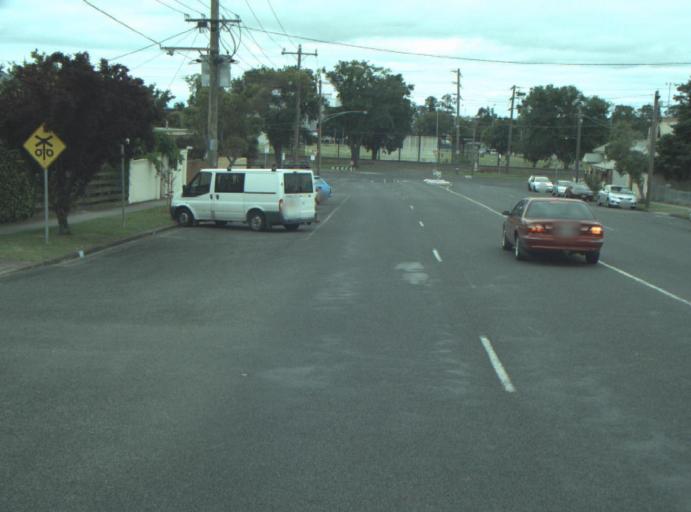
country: AU
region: Victoria
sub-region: Greater Geelong
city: Geelong
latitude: -38.1536
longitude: 144.3550
